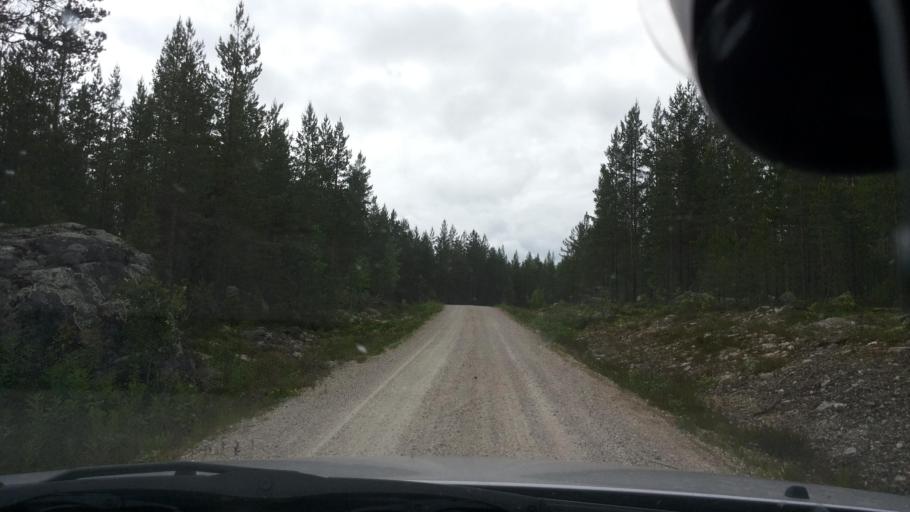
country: SE
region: Gaevleborg
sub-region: Ovanakers Kommun
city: Edsbyn
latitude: 61.4911
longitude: 15.3250
